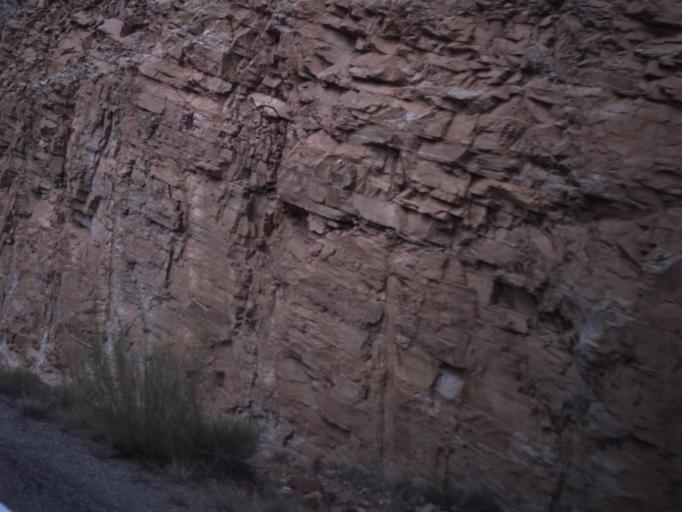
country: US
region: Utah
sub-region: San Juan County
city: Blanding
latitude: 37.2637
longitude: -109.6556
